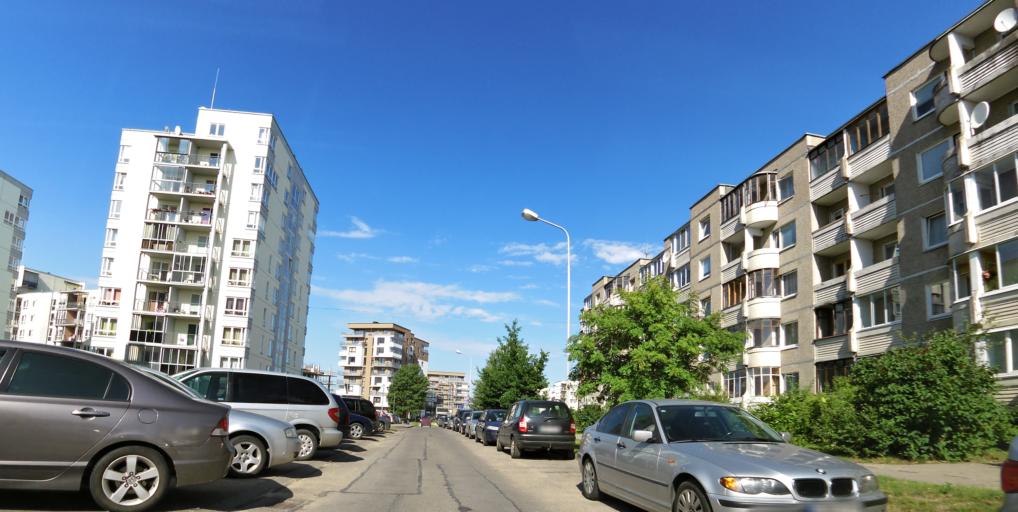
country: LT
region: Vilnius County
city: Pilaite
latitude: 54.7047
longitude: 25.1767
